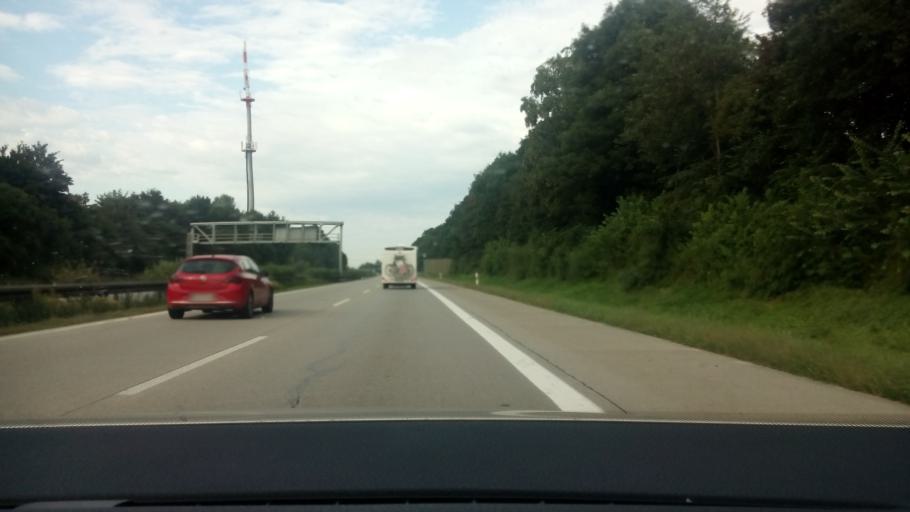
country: DE
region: Bavaria
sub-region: Upper Bavaria
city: Unterschleissheim
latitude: 48.2894
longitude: 11.5649
